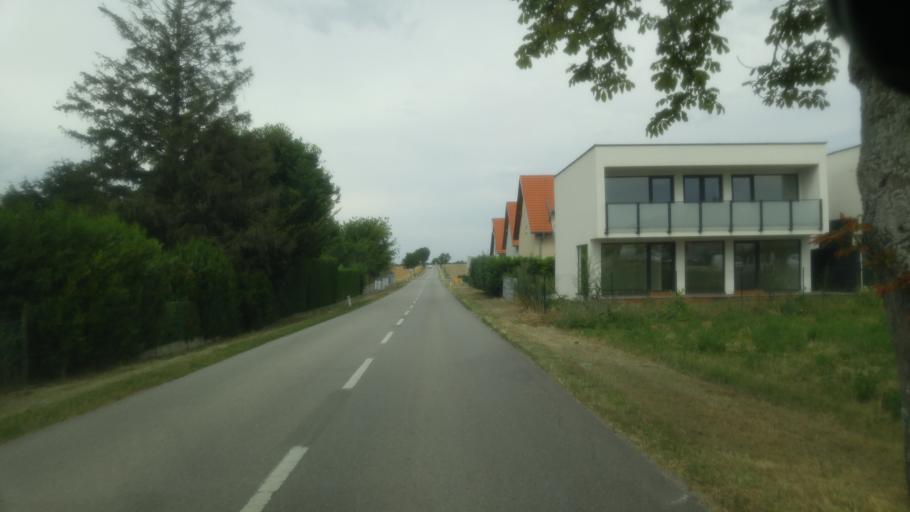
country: AT
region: Lower Austria
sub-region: Politischer Bezirk Wien-Umgebung
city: Moosbrunn
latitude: 48.0463
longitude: 16.4530
